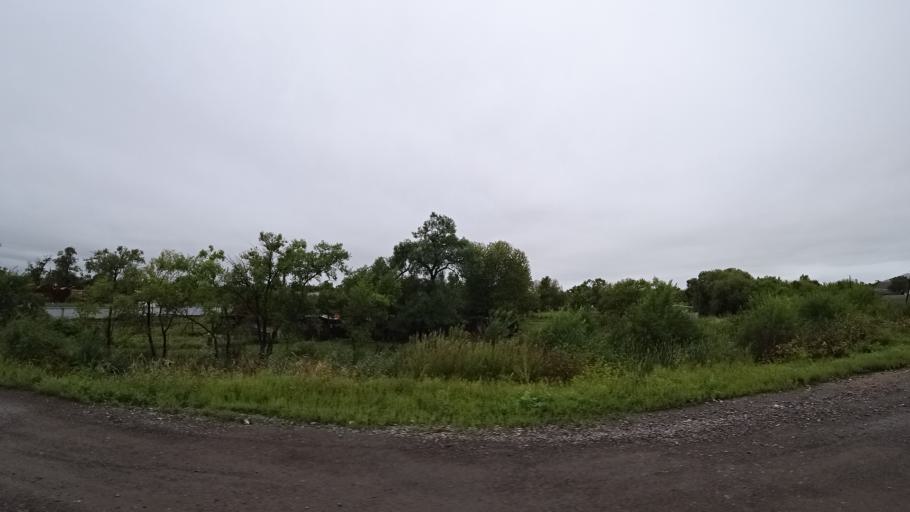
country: RU
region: Primorskiy
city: Monastyrishche
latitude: 44.2128
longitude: 132.4494
